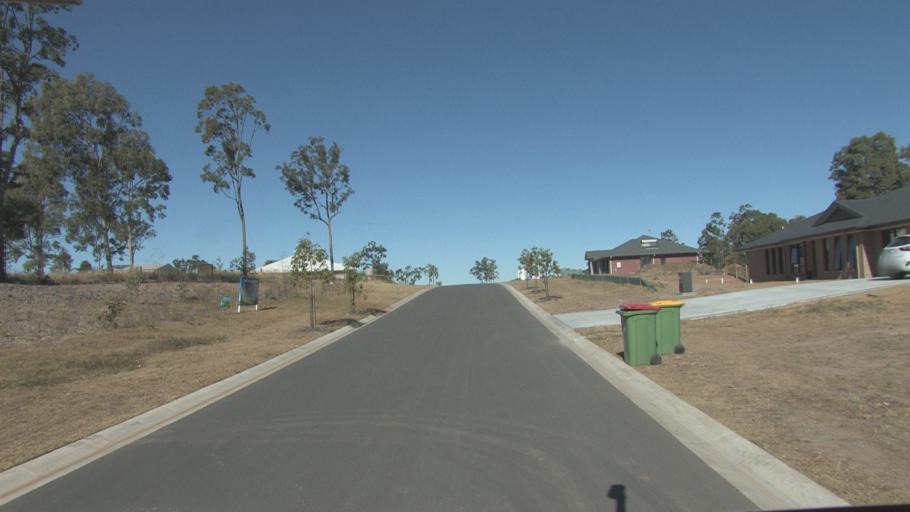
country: AU
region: Queensland
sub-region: Logan
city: North Maclean
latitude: -27.7548
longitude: 152.9432
